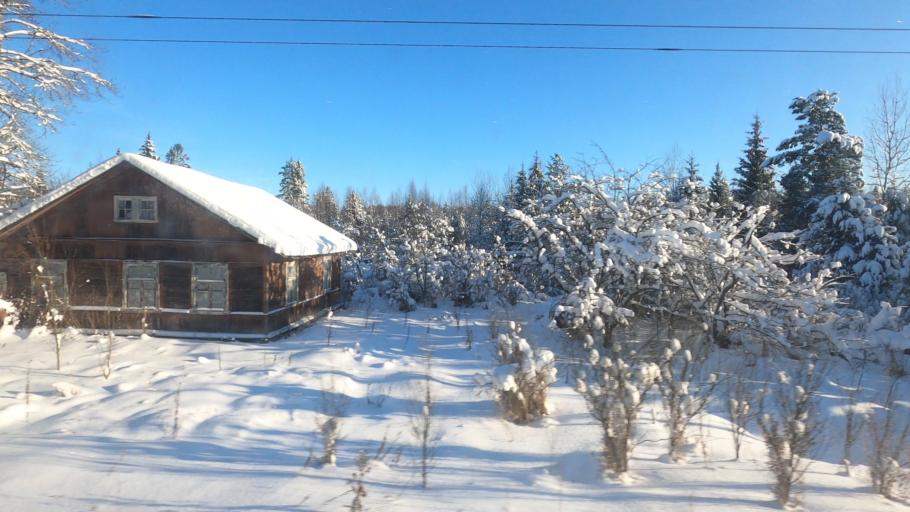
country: RU
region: Moskovskaya
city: Verbilki
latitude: 56.5291
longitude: 37.5594
